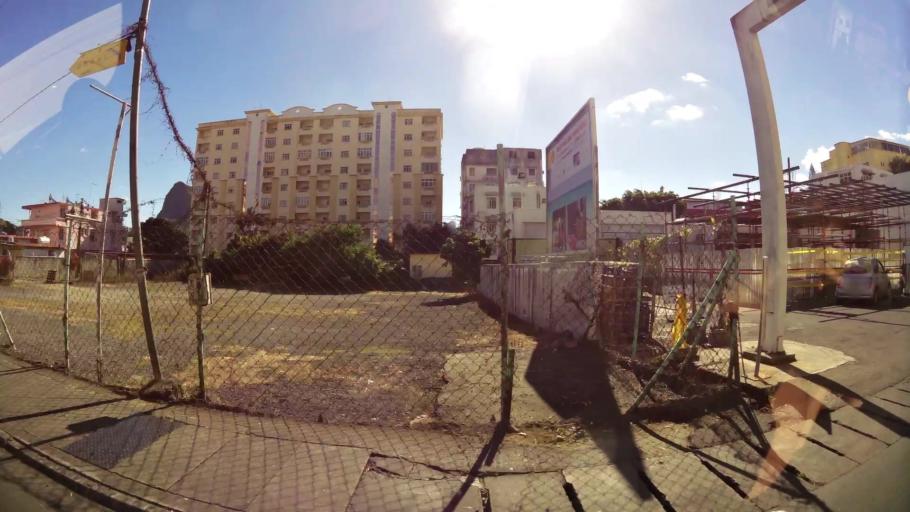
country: MU
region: Plaines Wilhems
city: Quatre Bornes
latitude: -20.2668
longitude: 57.4782
